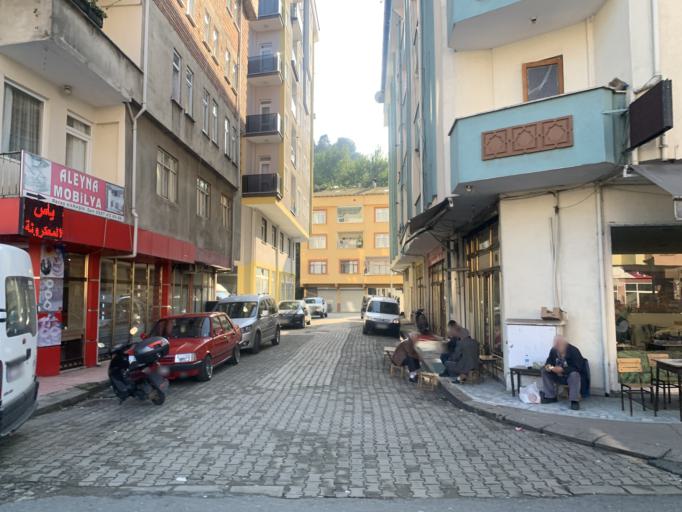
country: TR
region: Trabzon
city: Of
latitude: 40.9429
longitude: 40.2640
